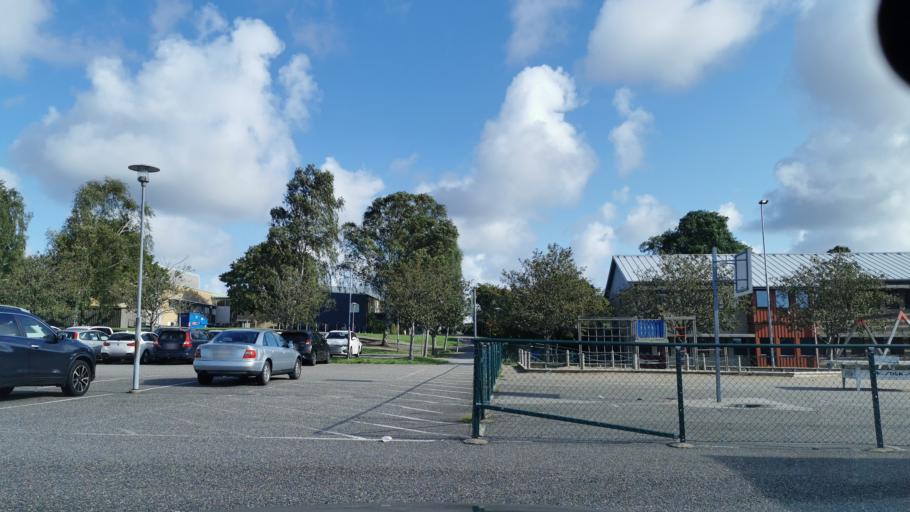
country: SE
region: Vaestra Goetaland
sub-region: Goteborg
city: Majorna
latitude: 57.6482
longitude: 11.9280
